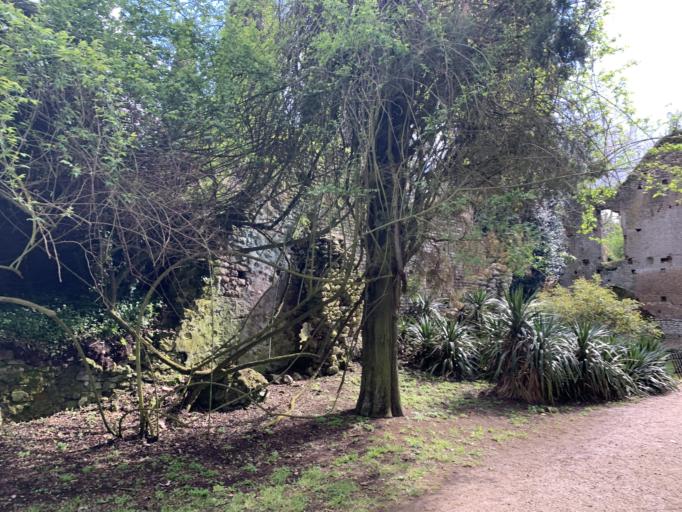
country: IT
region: Latium
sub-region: Provincia di Latina
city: Norma
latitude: 41.5814
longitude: 12.9534
